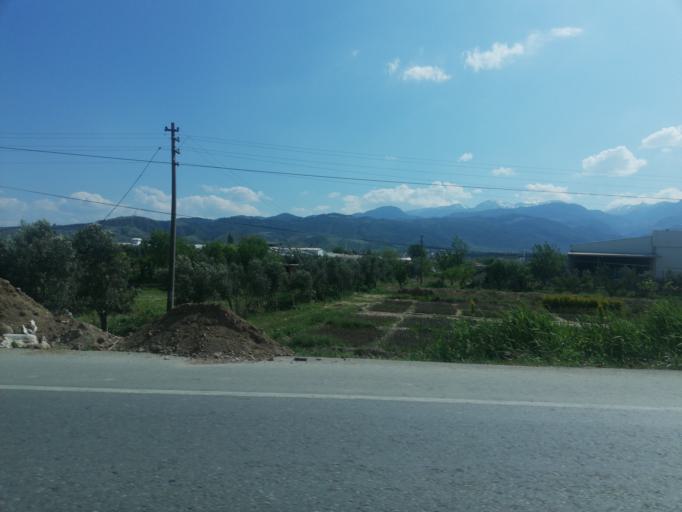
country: TR
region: Manisa
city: Alasehir
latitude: 38.3595
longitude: 28.5345
